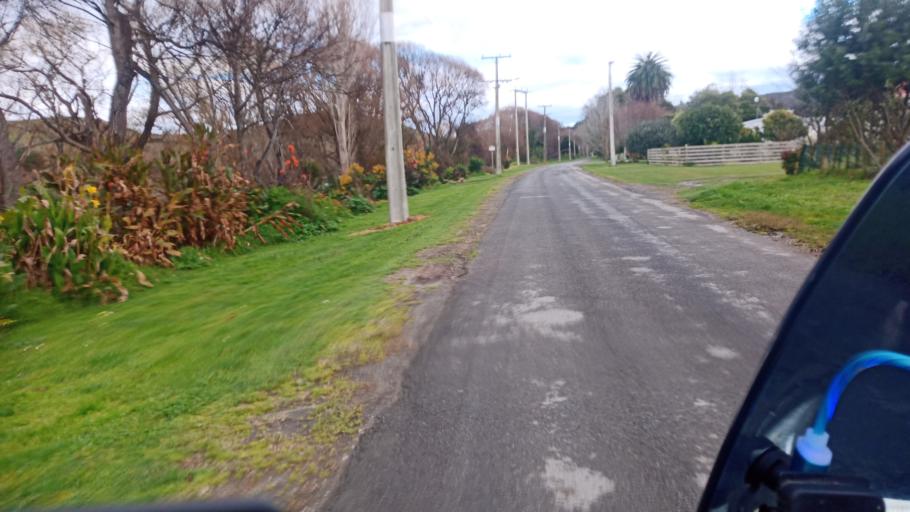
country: NZ
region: Gisborne
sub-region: Gisborne District
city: Gisborne
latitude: -38.3738
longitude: 178.2931
